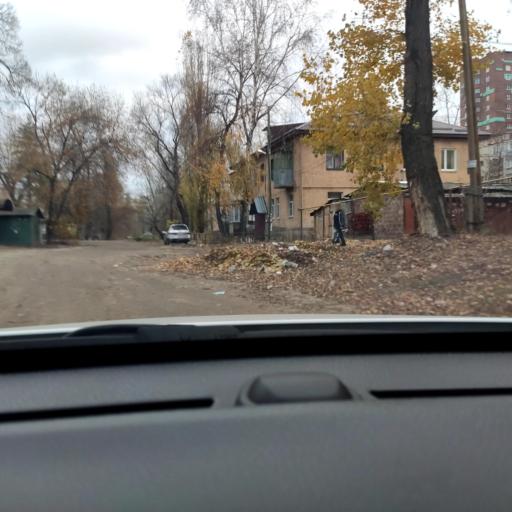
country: RU
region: Voronezj
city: Voronezh
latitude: 51.7238
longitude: 39.2608
